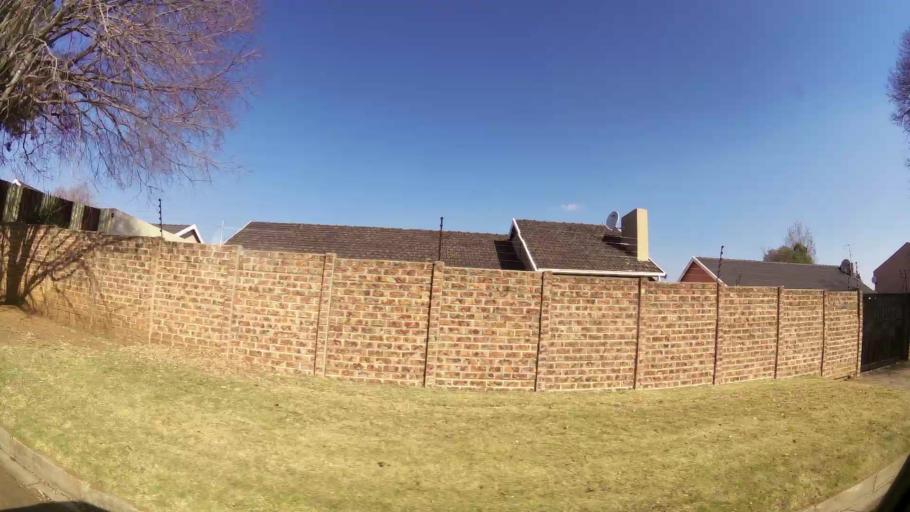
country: ZA
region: Gauteng
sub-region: City of Johannesburg Metropolitan Municipality
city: Johannesburg
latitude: -26.2554
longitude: 28.0002
